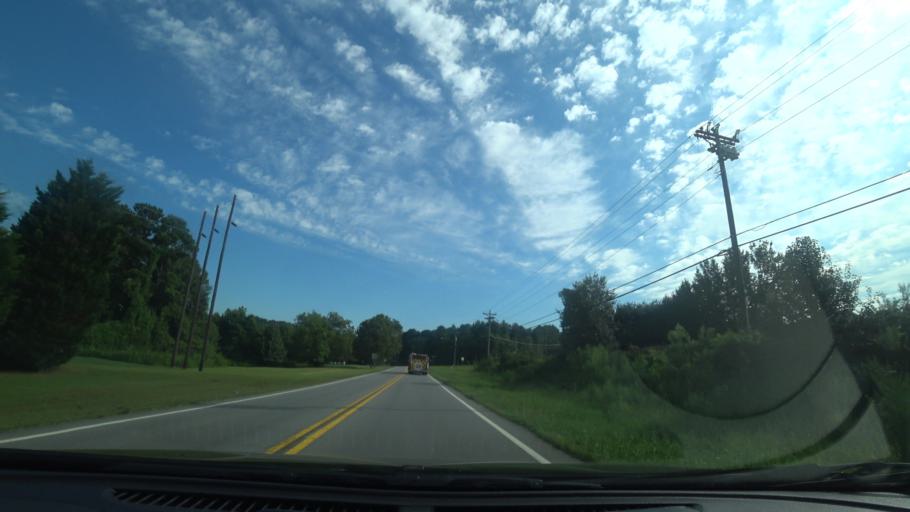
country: US
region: Georgia
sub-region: Gwinnett County
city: Grayson
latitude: 33.8397
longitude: -83.9595
